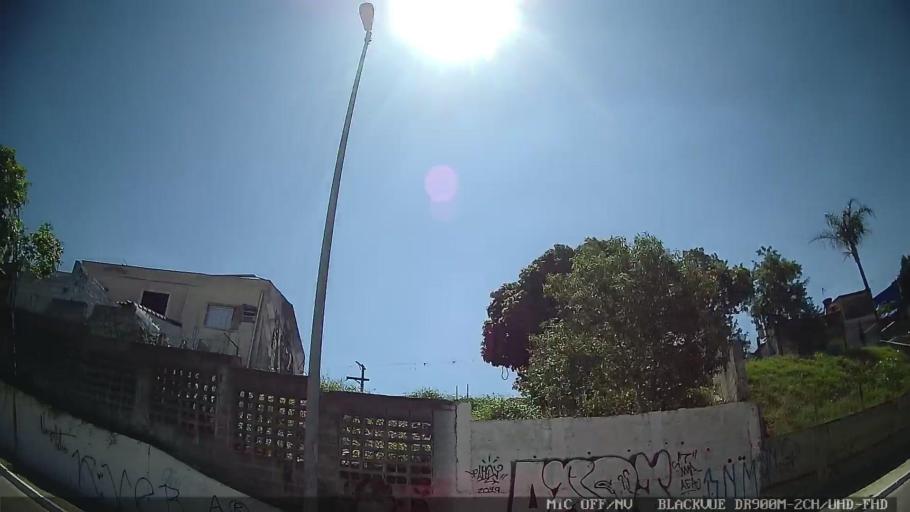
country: BR
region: Sao Paulo
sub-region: Sao Caetano Do Sul
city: Sao Caetano do Sul
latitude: -23.5727
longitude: -46.5199
